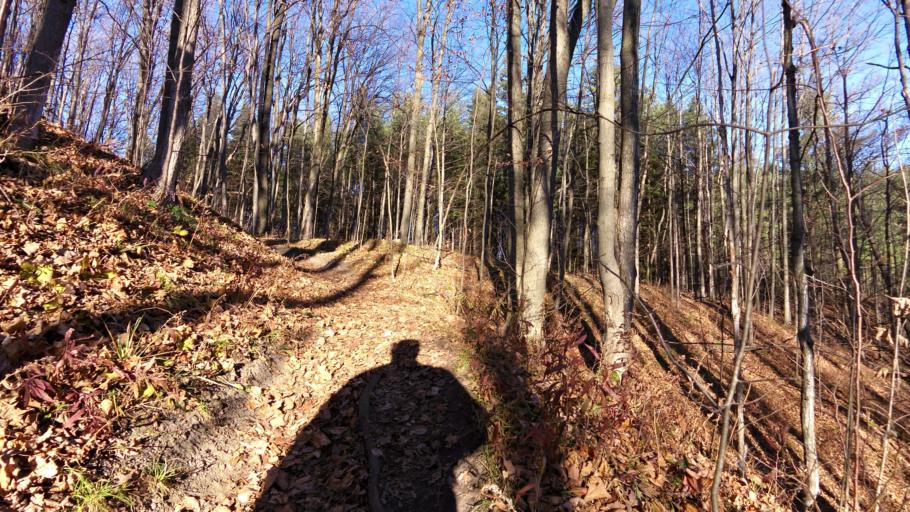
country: CA
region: Ontario
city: Orangeville
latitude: 43.9916
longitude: -80.0561
